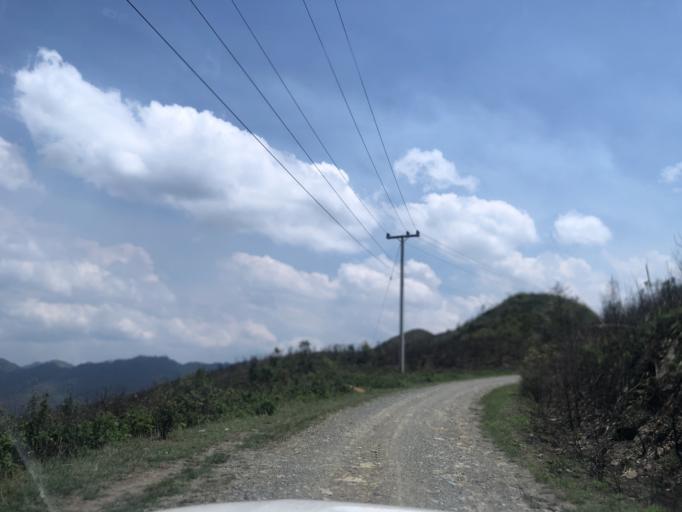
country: LA
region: Phongsali
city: Phongsali
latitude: 21.4163
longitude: 102.1852
